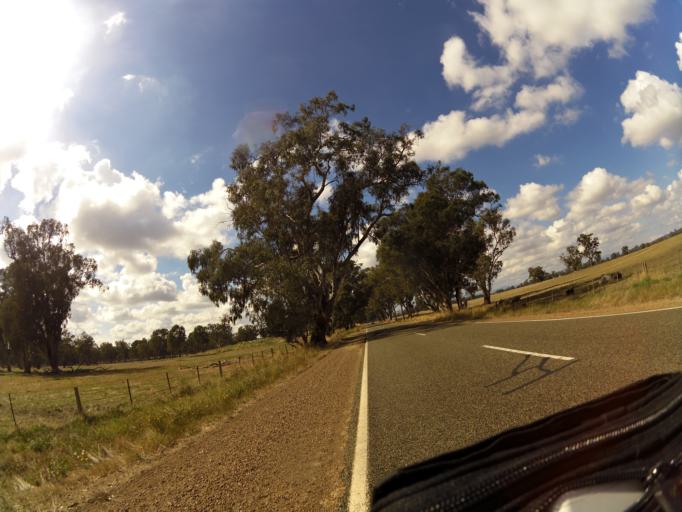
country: AU
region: Victoria
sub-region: Benalla
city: Benalla
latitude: -36.6172
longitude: 146.0298
